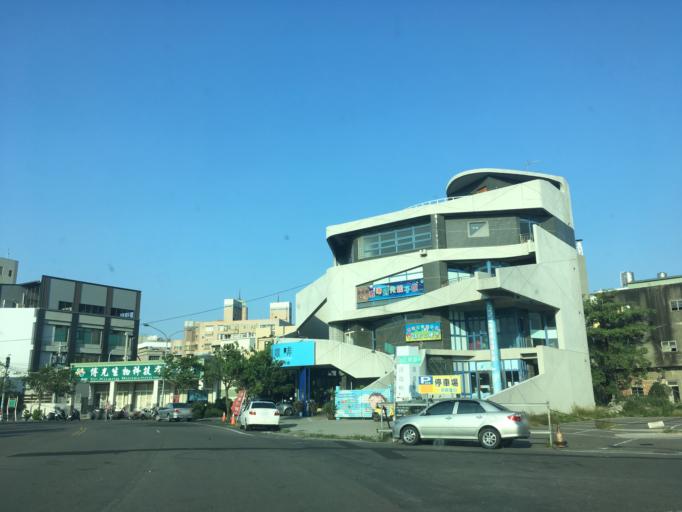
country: TW
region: Taiwan
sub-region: Changhua
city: Chang-hua
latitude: 24.0596
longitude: 120.4359
